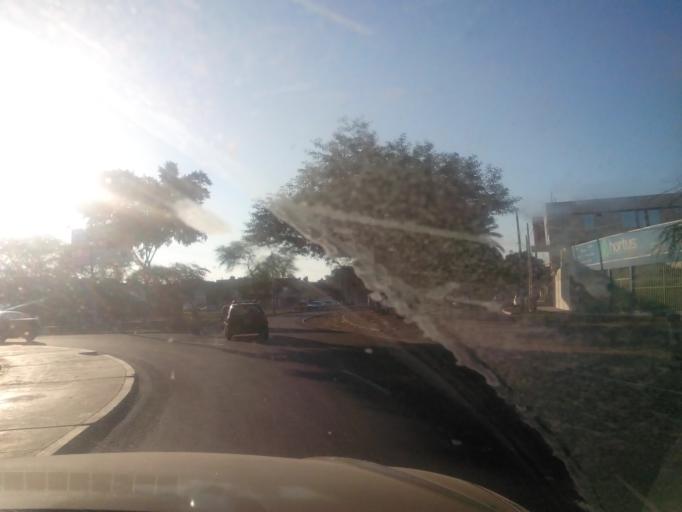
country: PE
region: Ica
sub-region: Provincia de Ica
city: Ica
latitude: -14.0717
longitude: -75.7383
